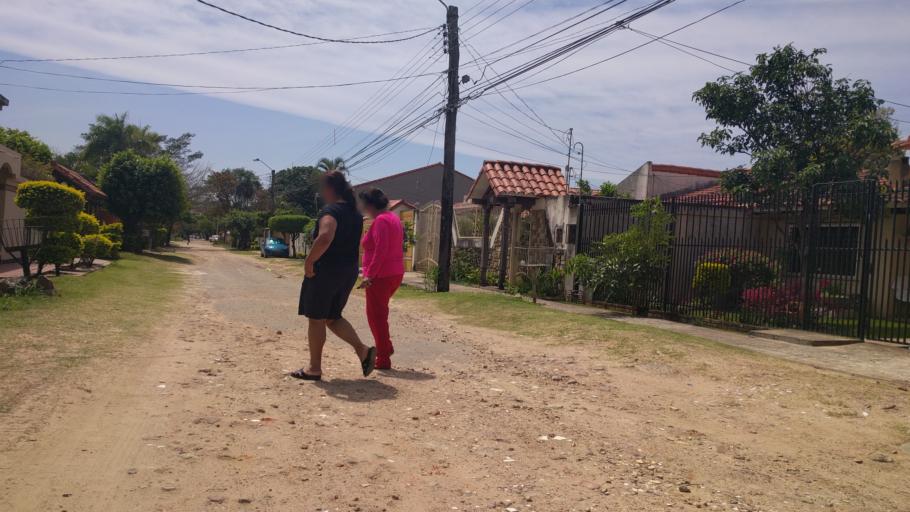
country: BO
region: Santa Cruz
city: Santa Cruz de la Sierra
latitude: -17.8176
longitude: -63.2237
